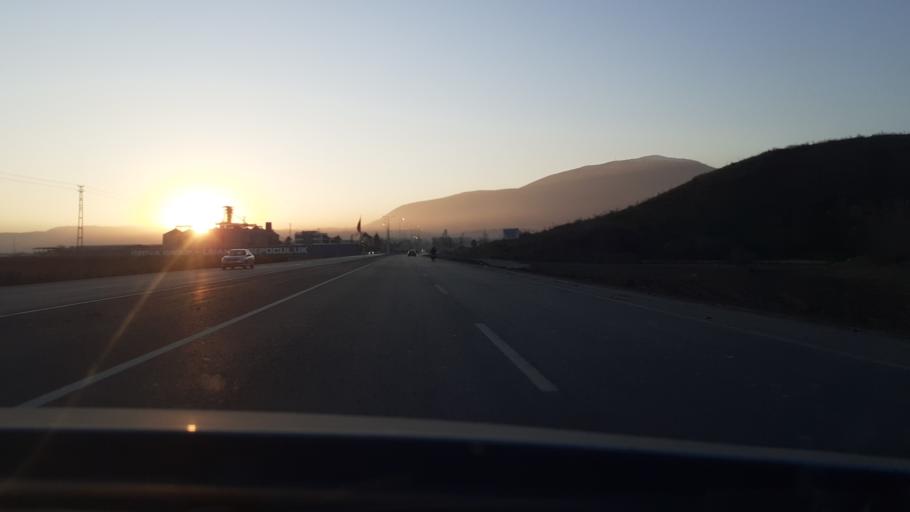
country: TR
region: Hatay
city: Kirikhan
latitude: 36.5025
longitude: 36.3938
